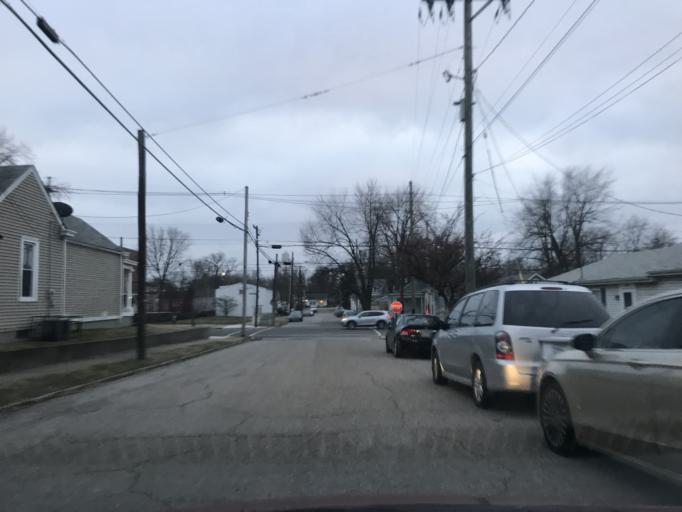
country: US
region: Kentucky
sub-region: Jefferson County
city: Audubon Park
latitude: 38.2240
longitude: -85.7402
